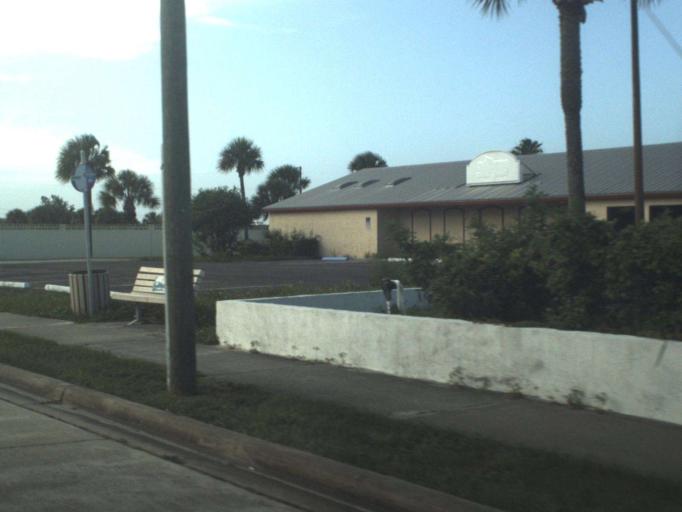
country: US
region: Florida
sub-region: Volusia County
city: Port Orange
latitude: 29.1525
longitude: -80.9919
